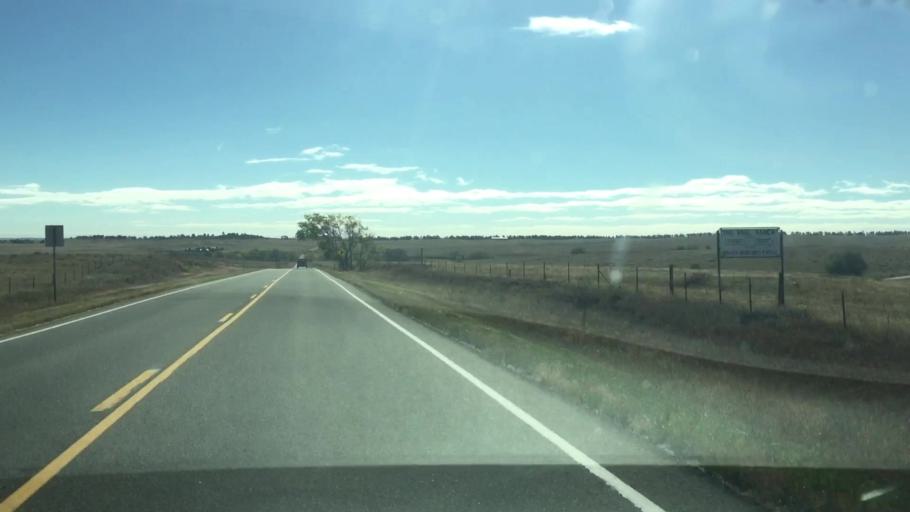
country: US
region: Colorado
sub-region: Elbert County
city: Kiowa
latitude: 39.3265
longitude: -104.3976
